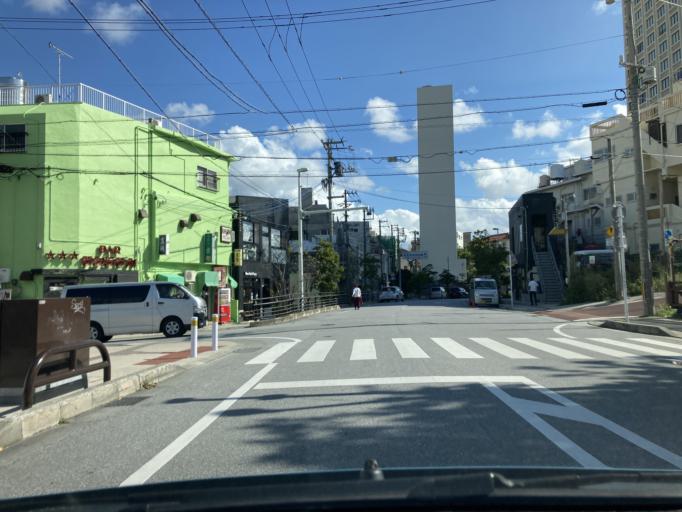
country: JP
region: Okinawa
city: Naha-shi
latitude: 26.2154
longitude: 127.6901
